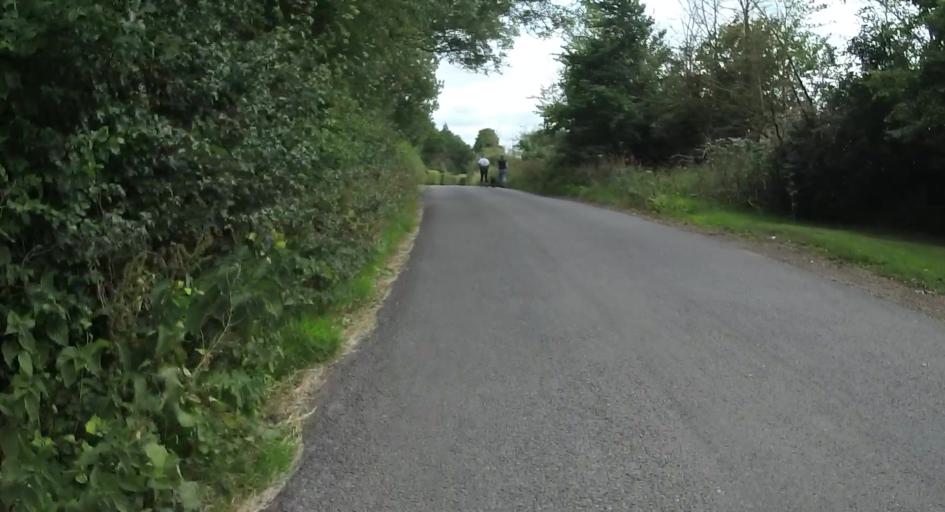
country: GB
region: England
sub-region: West Berkshire
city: Stratfield Mortimer
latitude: 51.3443
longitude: -1.0422
